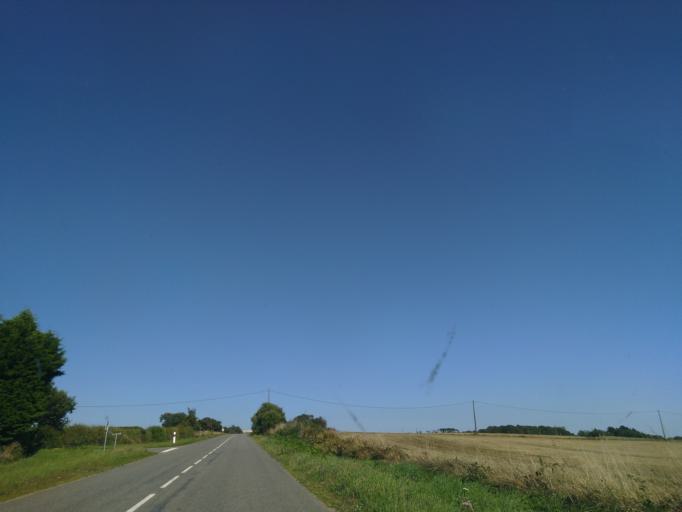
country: FR
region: Brittany
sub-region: Departement du Finistere
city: Le Faou
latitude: 48.2654
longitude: -4.2247
